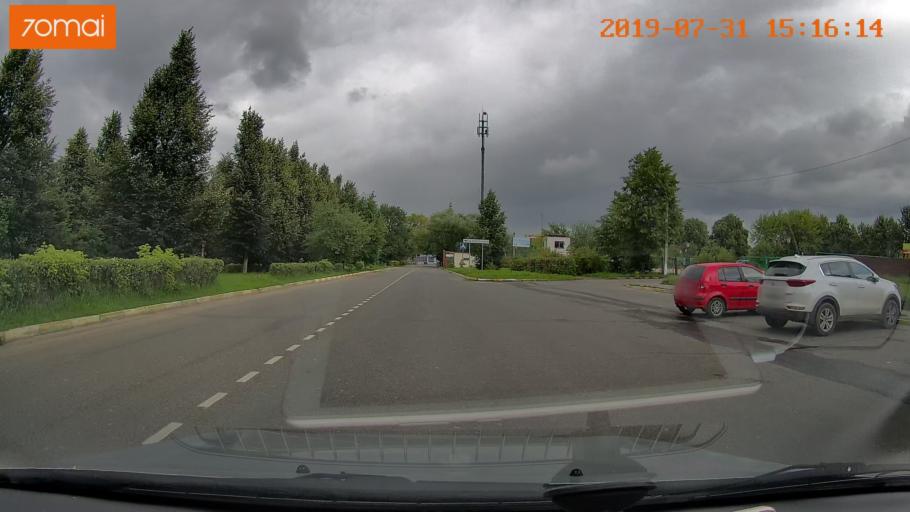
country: RU
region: Moskovskaya
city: Voskresensk
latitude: 55.3156
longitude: 38.6598
